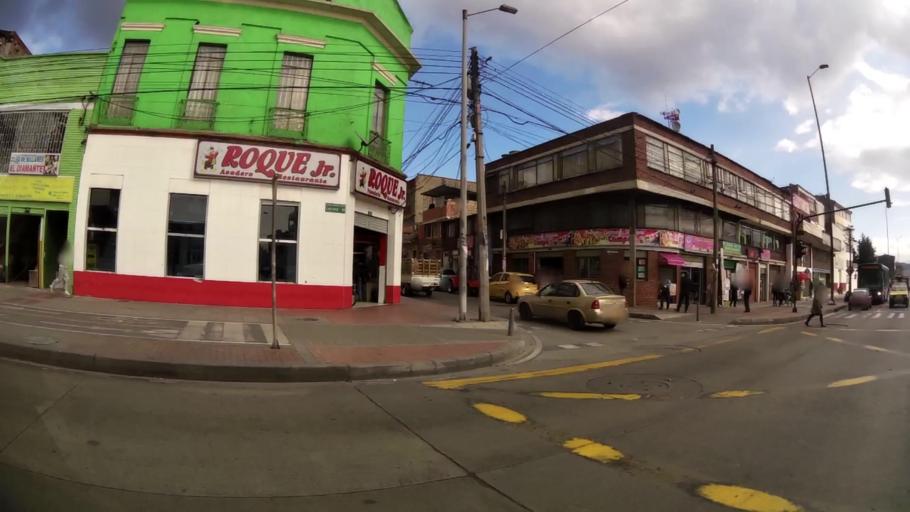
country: CO
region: Bogota D.C.
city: Bogota
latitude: 4.5912
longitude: -74.0836
